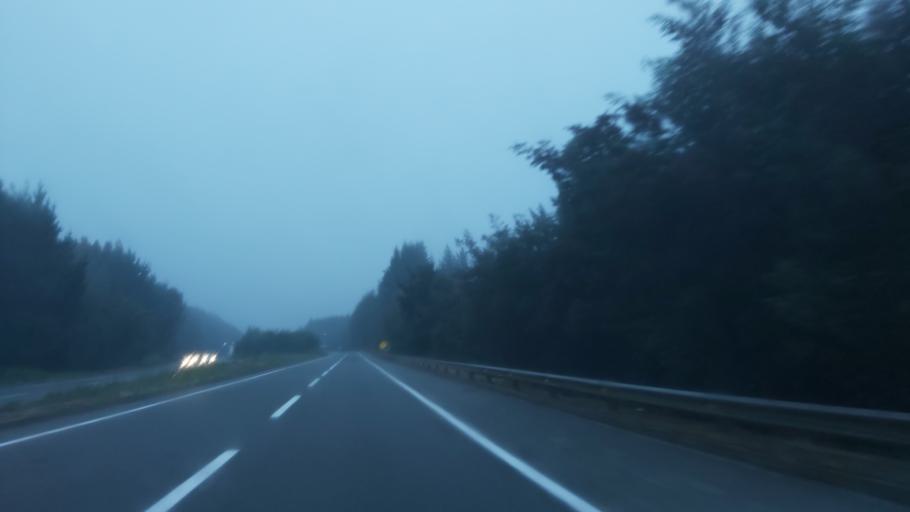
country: CL
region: Biobio
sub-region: Provincia de Concepcion
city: Penco
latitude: -36.7442
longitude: -72.9144
